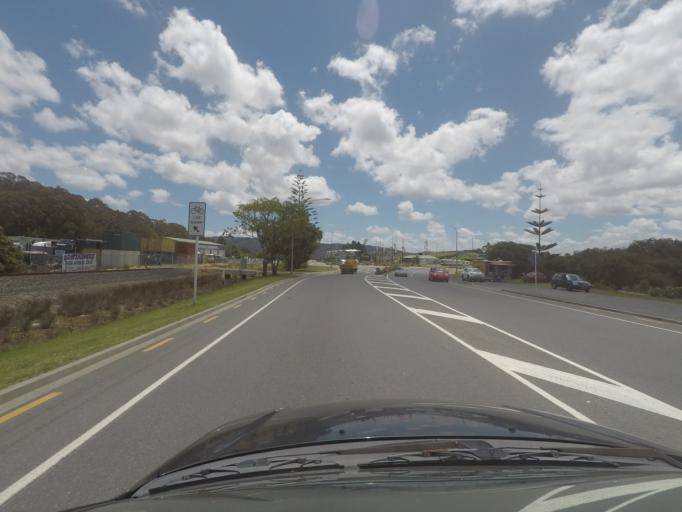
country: NZ
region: Northland
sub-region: Whangarei
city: Whangarei
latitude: -35.7378
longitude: 174.3332
